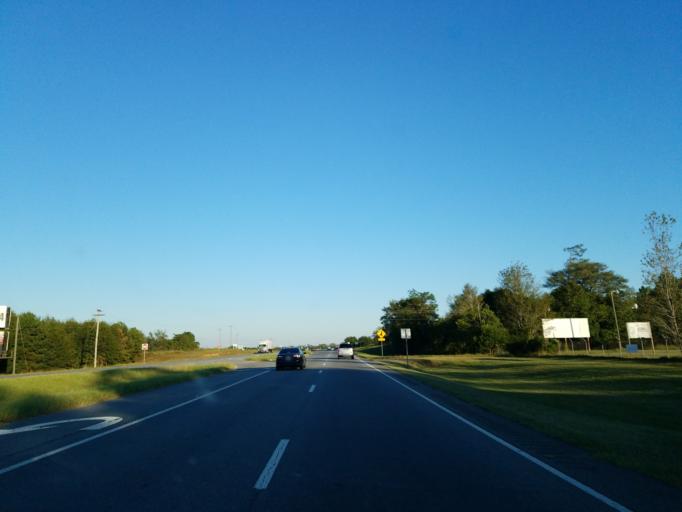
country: US
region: Georgia
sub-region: Worth County
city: Sylvester
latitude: 31.5058
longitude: -83.7291
